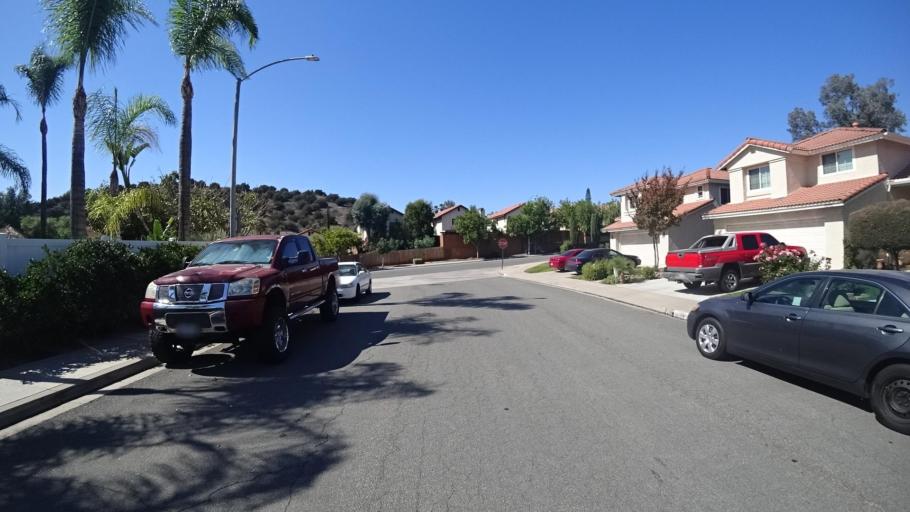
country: US
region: California
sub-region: San Diego County
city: Rancho San Diego
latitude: 32.7527
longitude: -116.9349
